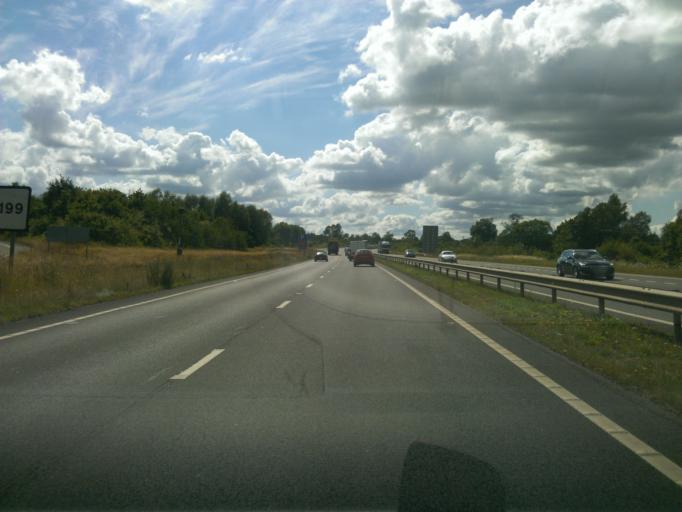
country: GB
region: England
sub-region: Northamptonshire
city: Long Buckby
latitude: 52.3963
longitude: -1.0322
